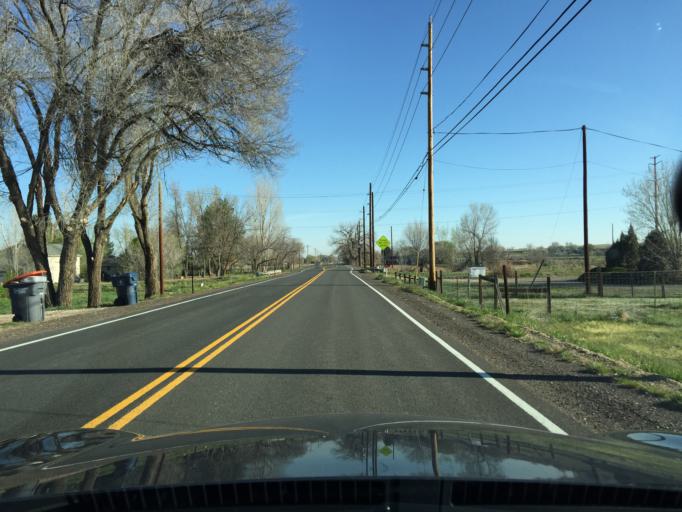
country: US
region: Colorado
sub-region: Boulder County
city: Erie
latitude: 40.0568
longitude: -105.0554
